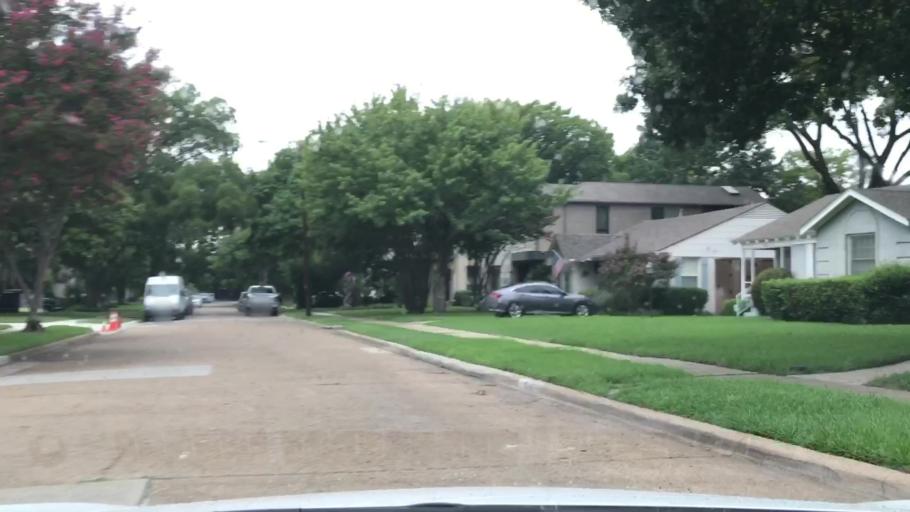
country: US
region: Texas
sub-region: Dallas County
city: University Park
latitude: 32.8543
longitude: -96.8283
